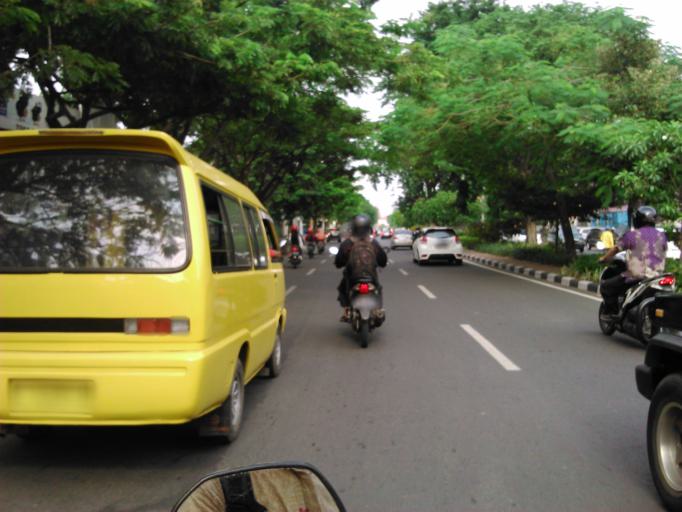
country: ID
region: East Java
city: Brongkalan
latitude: -7.2660
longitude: 112.7642
